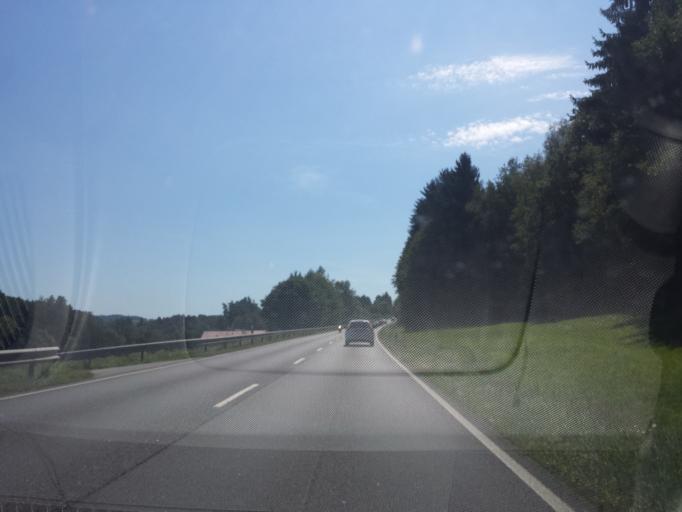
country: DE
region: Bavaria
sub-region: Upper Palatinate
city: Traitsching
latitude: 49.1326
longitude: 12.6527
